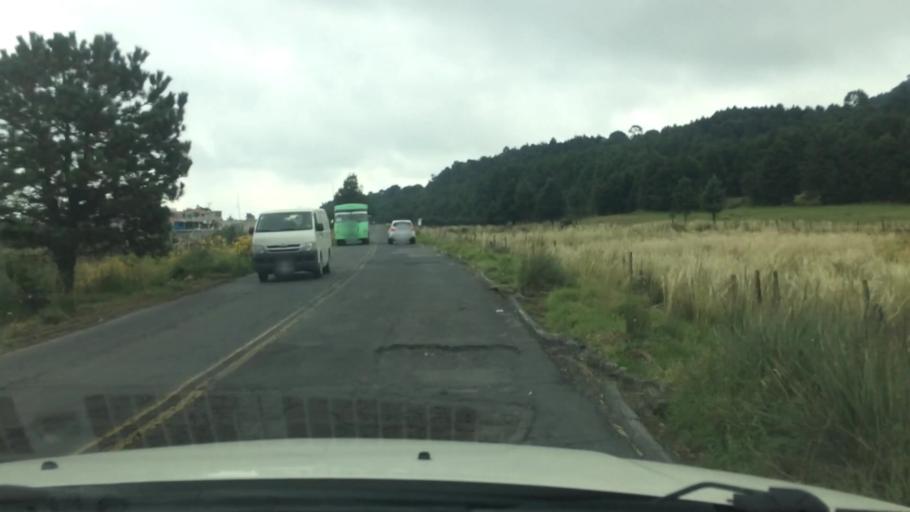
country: MX
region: Mexico City
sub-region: Tlalpan
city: Lomas de Tepemecatl
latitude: 19.2318
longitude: -99.2275
